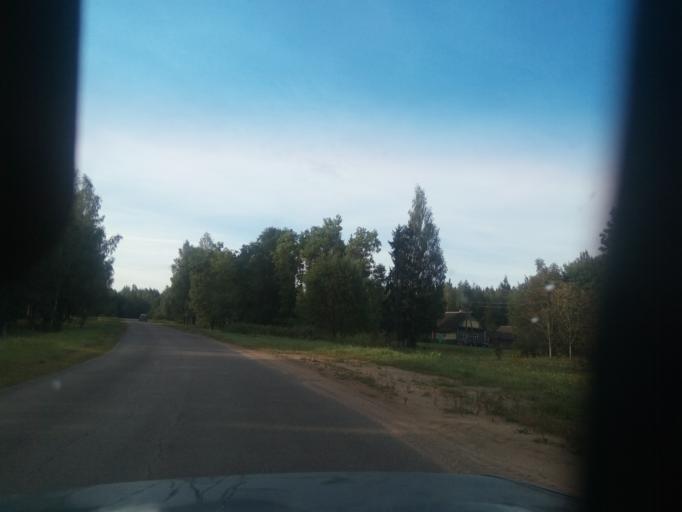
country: BY
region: Vitebsk
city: Dzisna
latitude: 55.6539
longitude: 28.3220
